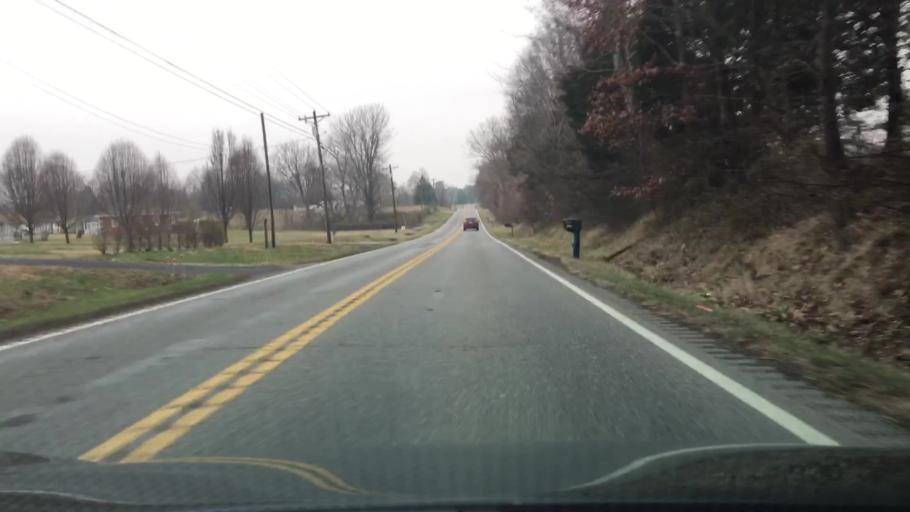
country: US
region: Kentucky
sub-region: Livingston County
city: Ledbetter
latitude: 36.9664
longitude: -88.4431
